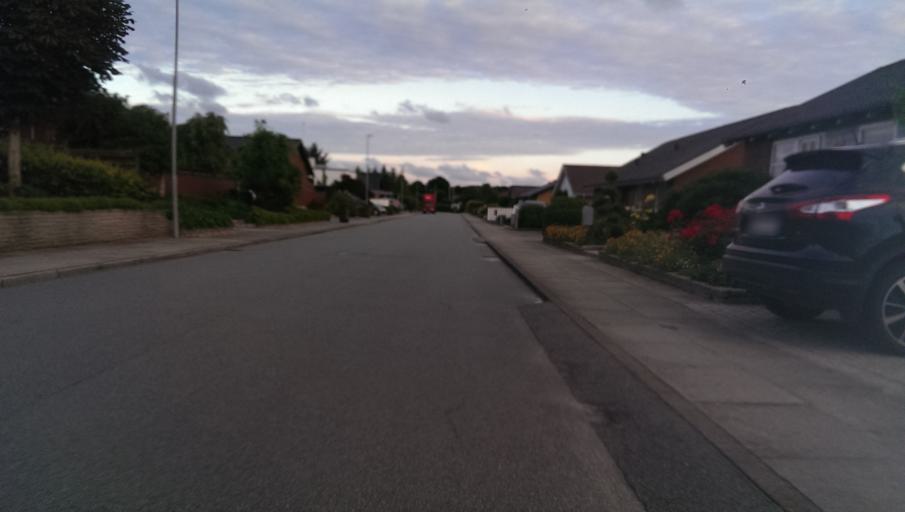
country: DK
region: South Denmark
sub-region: Esbjerg Kommune
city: Tjaereborg
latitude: 55.4714
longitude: 8.5724
